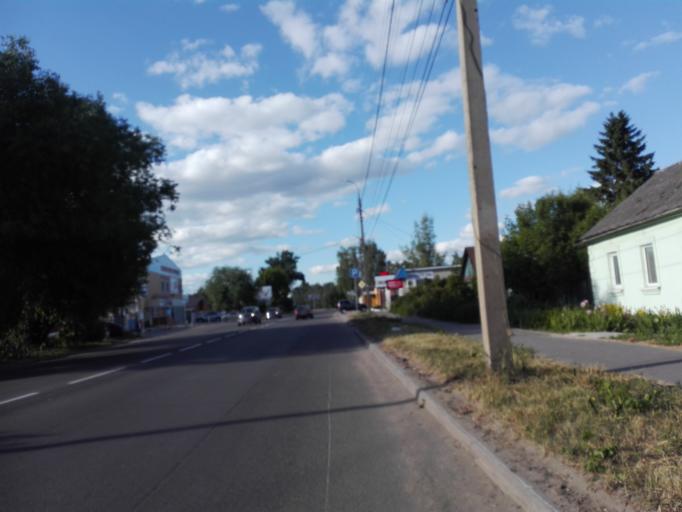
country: RU
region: Orjol
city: Orel
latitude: 52.9449
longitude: 36.0752
